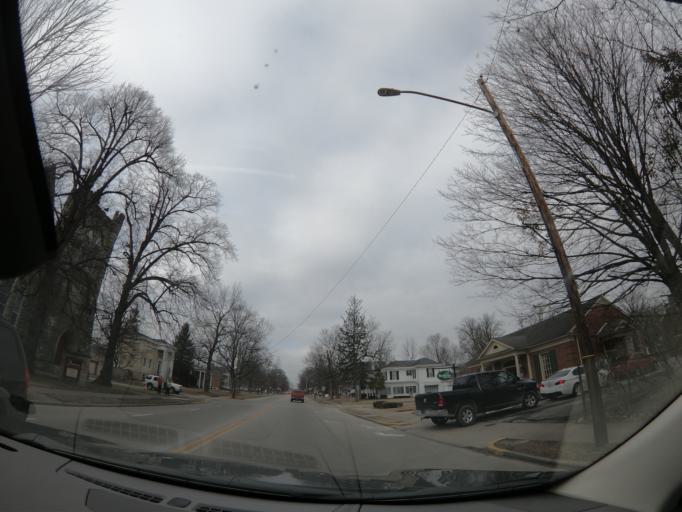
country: US
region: Kentucky
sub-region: Nelson County
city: Bardstown
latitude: 37.8131
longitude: -85.4656
